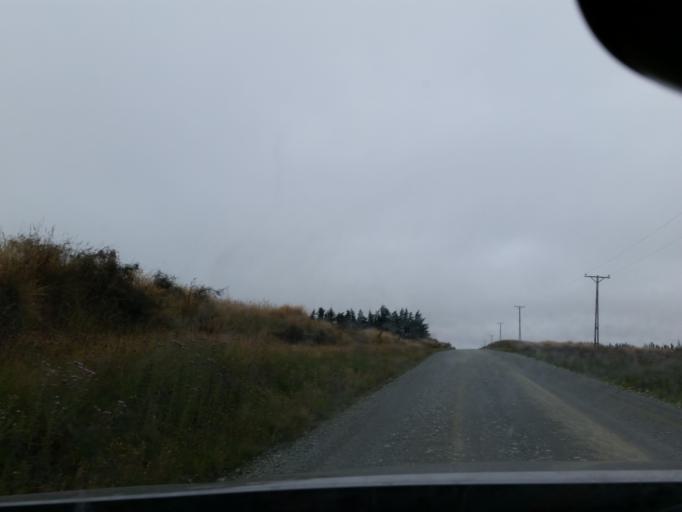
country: NZ
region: Southland
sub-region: Southland District
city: Te Anau
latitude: -45.5042
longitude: 168.1156
